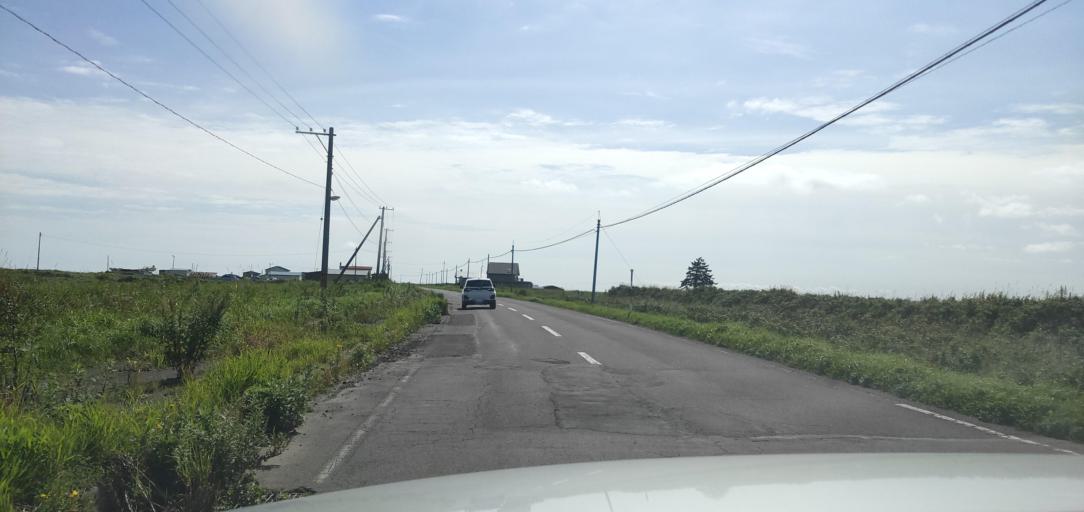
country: JP
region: Hokkaido
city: Shibetsu
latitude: 43.6299
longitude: 145.1912
